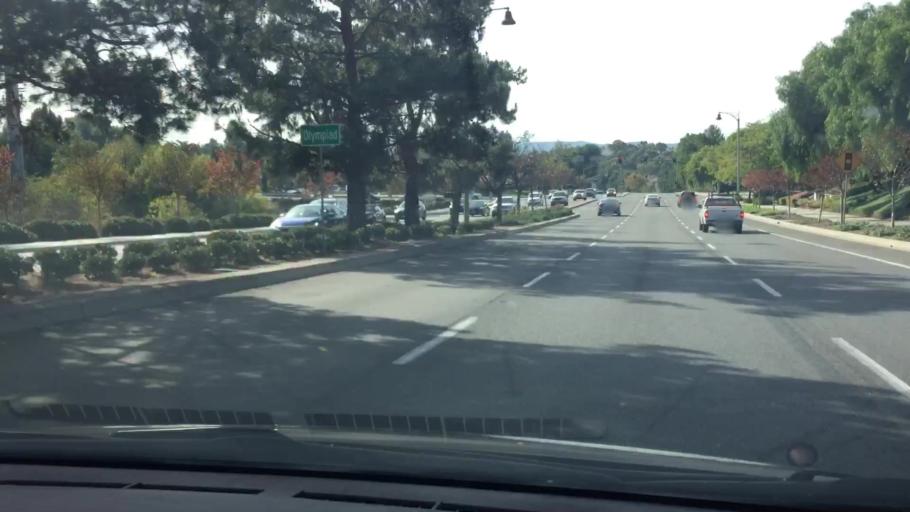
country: US
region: California
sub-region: Orange County
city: Rancho Santa Margarita
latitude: 33.6300
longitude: -117.6328
